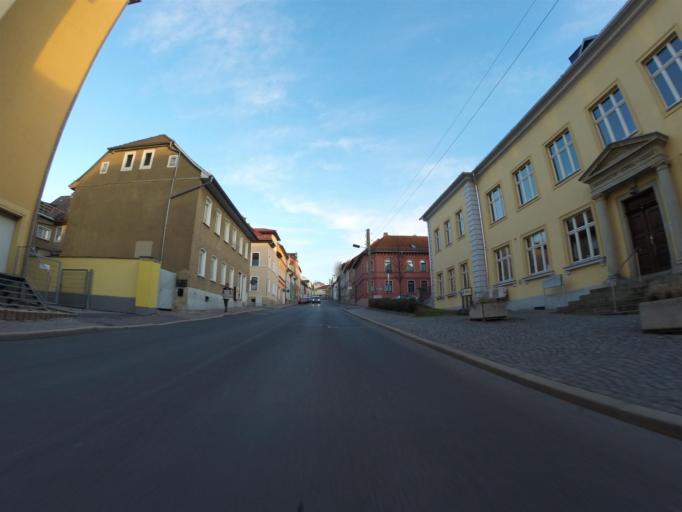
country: DE
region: Thuringia
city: Apolda
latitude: 51.0248
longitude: 11.5188
